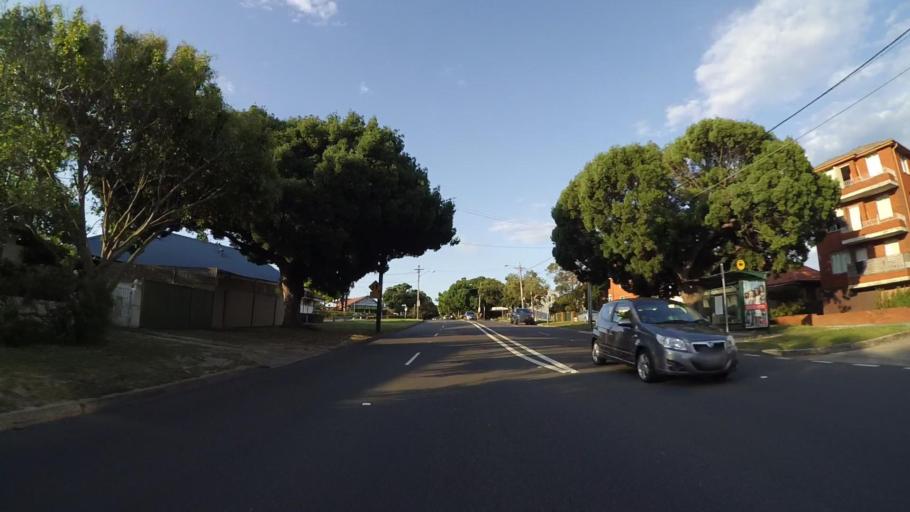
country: AU
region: New South Wales
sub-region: Randwick
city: Daceyville
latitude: -33.9380
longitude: 151.2294
